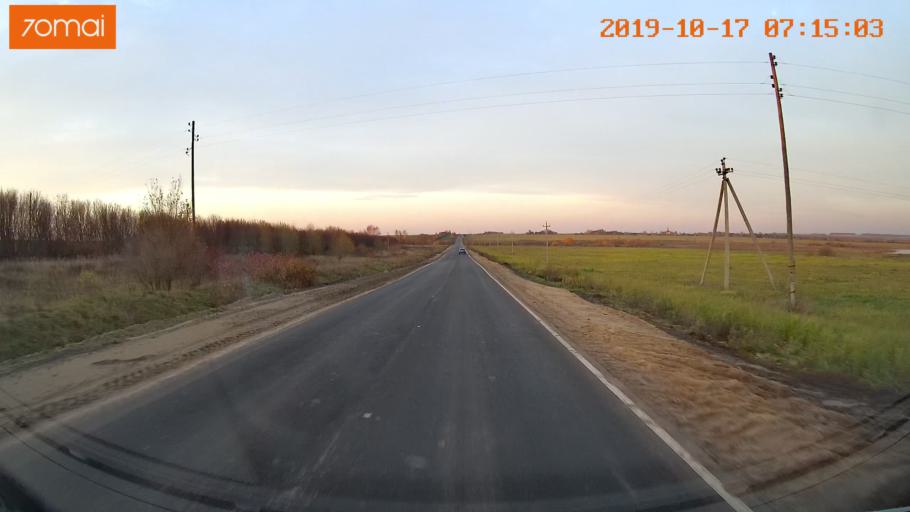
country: RU
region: Vladimir
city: Suzdal'
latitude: 56.3846
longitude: 40.2750
